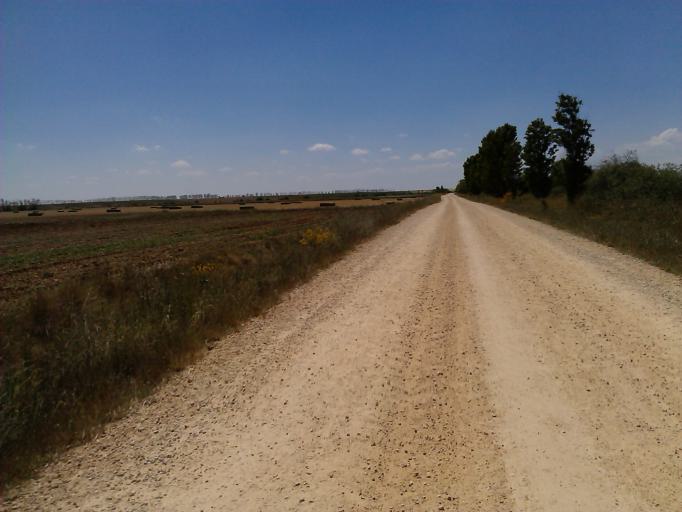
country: ES
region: Castille and Leon
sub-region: Provincia de Palencia
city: Bustillo del Paramo de Carrion
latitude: 42.3346
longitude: -4.7417
